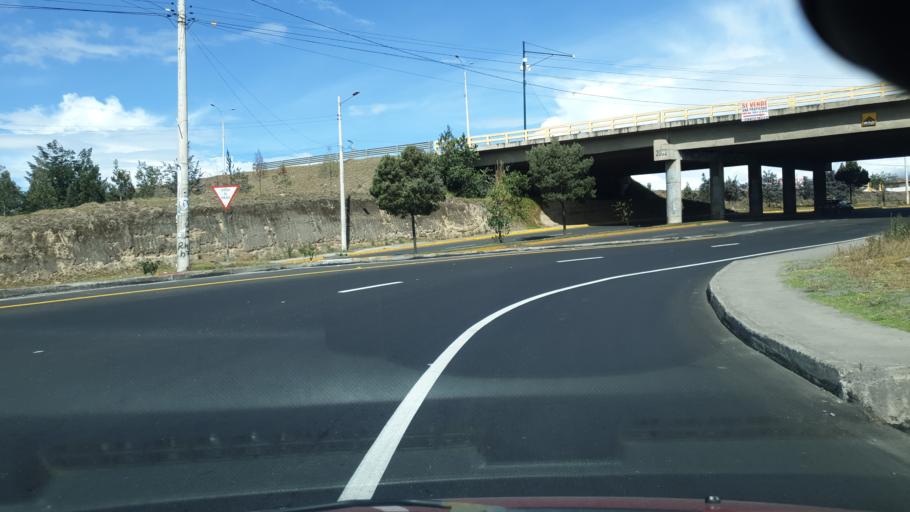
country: EC
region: Tungurahua
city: Ambato
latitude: -1.3031
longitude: -78.6376
